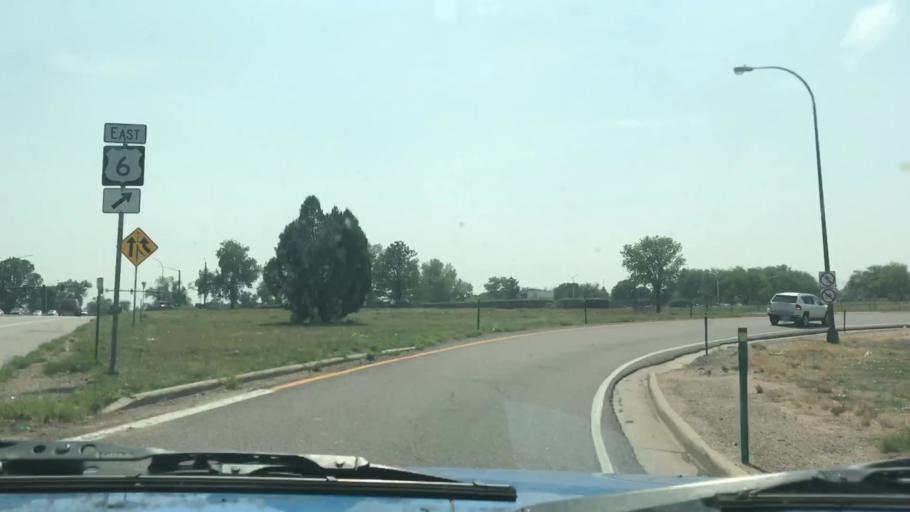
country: US
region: Colorado
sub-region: Jefferson County
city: Lakewood
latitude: 39.7246
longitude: -105.1099
